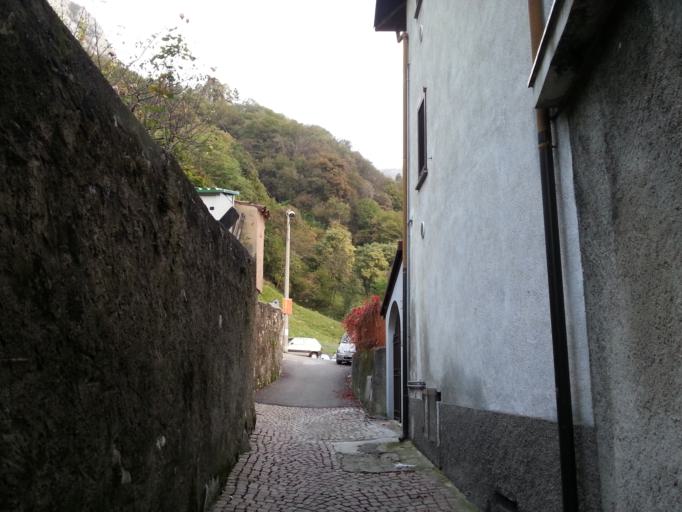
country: IT
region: Lombardy
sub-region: Provincia di Lecco
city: Ballabio
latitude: 45.8804
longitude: 9.4063
